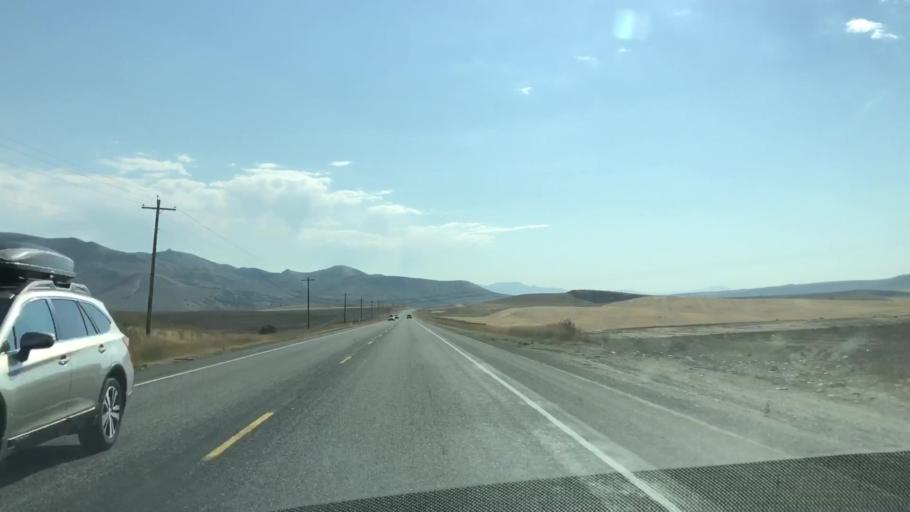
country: US
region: Idaho
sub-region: Madison County
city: Rexburg
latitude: 43.6086
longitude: -111.6785
